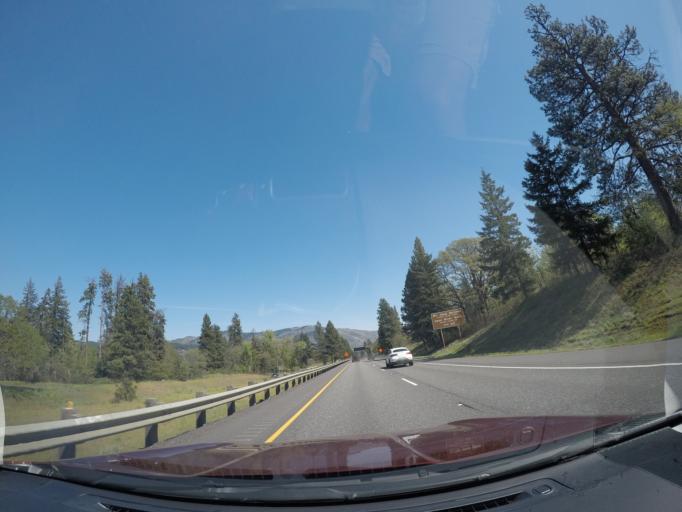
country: US
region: Oregon
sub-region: Hood River County
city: Hood River
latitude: 45.7127
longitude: -121.5331
